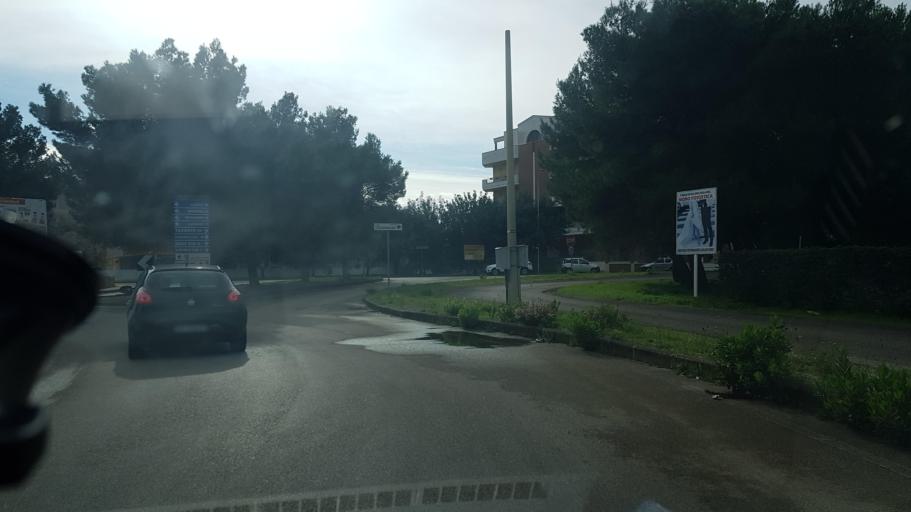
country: IT
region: Apulia
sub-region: Provincia di Brindisi
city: San Vito dei Normanni
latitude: 40.6656
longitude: 17.6990
